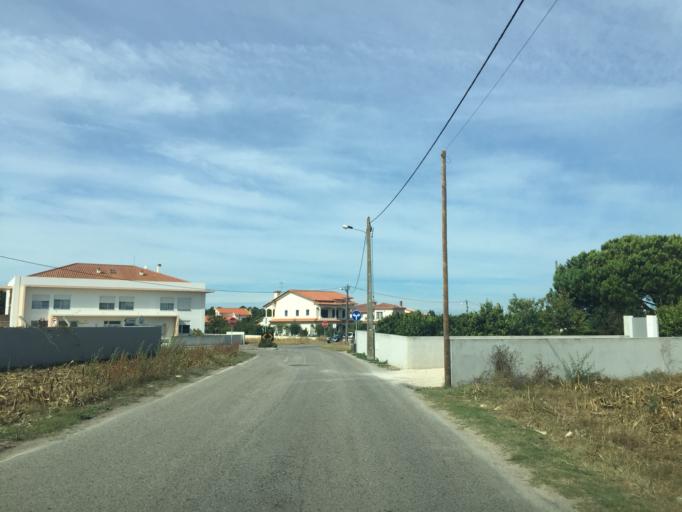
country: PT
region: Coimbra
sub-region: Figueira da Foz
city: Lavos
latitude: 40.0714
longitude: -8.8170
